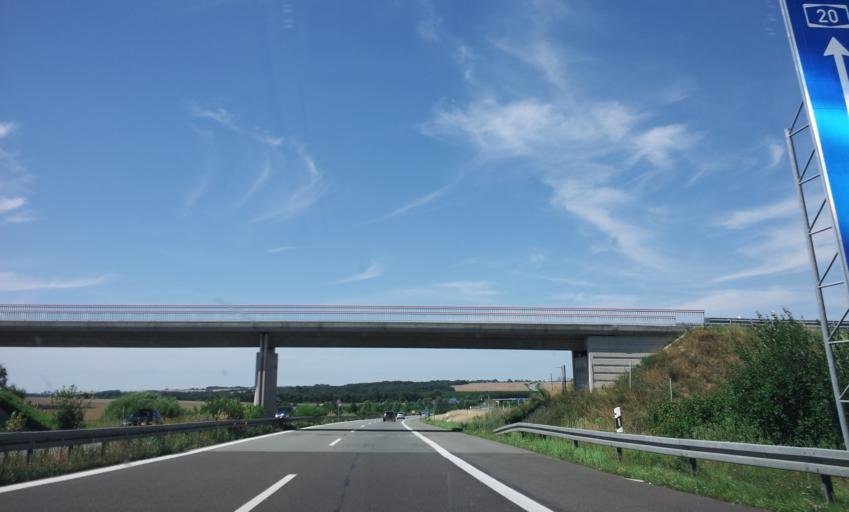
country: DE
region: Mecklenburg-Vorpommern
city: Neuenkirchen
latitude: 53.5779
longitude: 13.4325
